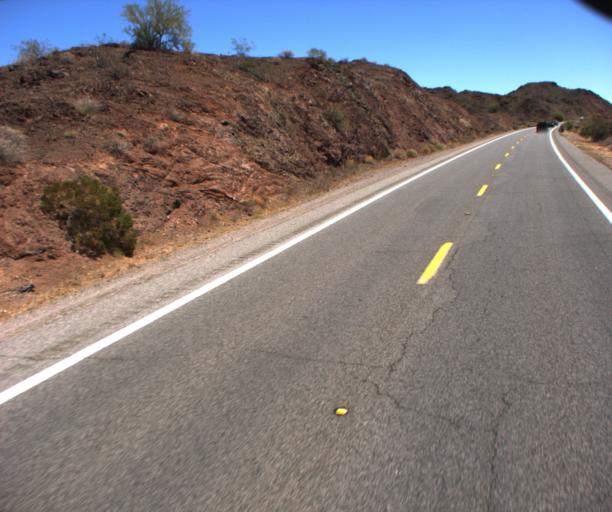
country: US
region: Arizona
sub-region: La Paz County
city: Cienega Springs
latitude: 34.3234
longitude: -114.1233
